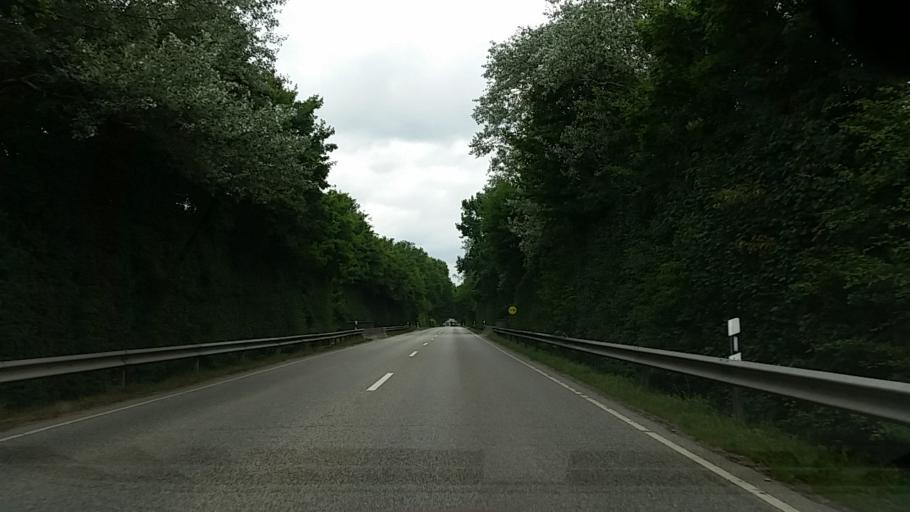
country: DE
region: Schleswig-Holstein
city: Tangstedt
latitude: 53.7065
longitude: 10.0651
